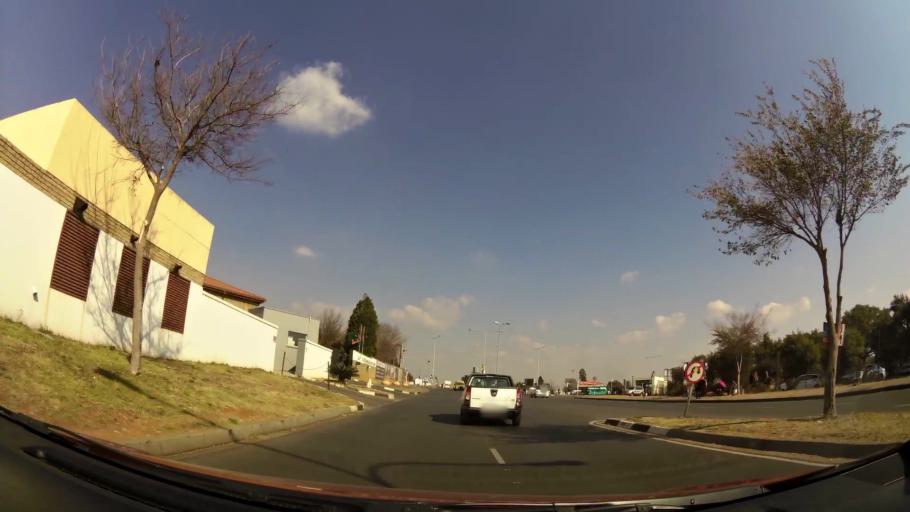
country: ZA
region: Gauteng
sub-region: City of Johannesburg Metropolitan Municipality
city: Soweto
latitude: -26.2579
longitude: 27.9351
